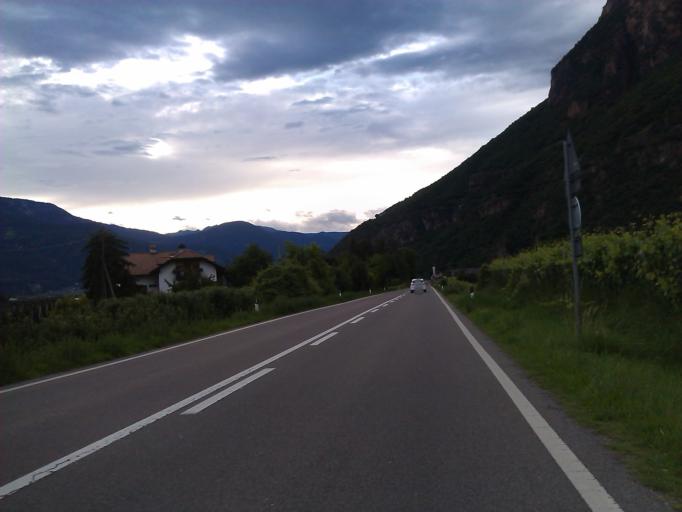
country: IT
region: Trentino-Alto Adige
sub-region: Bolzano
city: Bolzano
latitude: 46.4990
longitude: 11.3027
